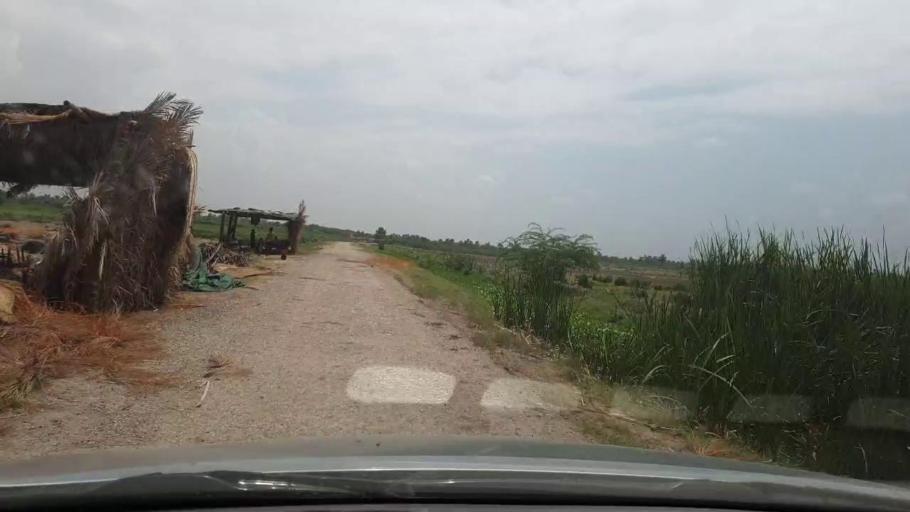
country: PK
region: Sindh
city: Kot Diji
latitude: 27.4264
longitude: 68.7617
